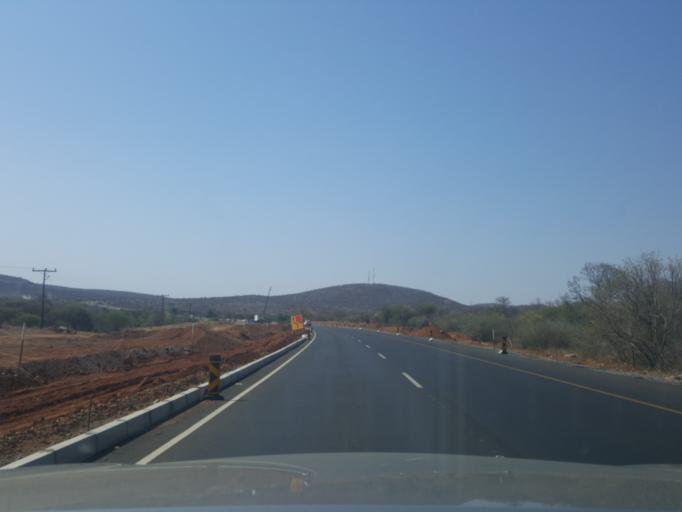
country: BW
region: Kweneng
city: Gabane
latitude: -24.7668
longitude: 25.8313
